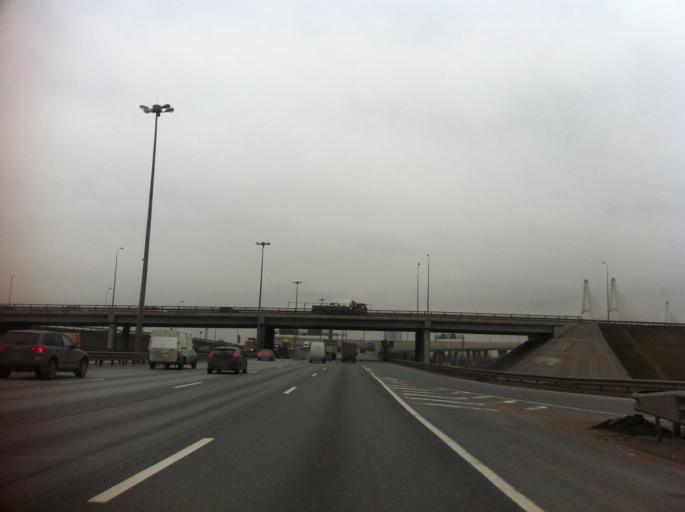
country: RU
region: Leningrad
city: Rybatskoye
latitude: 59.8574
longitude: 30.5116
